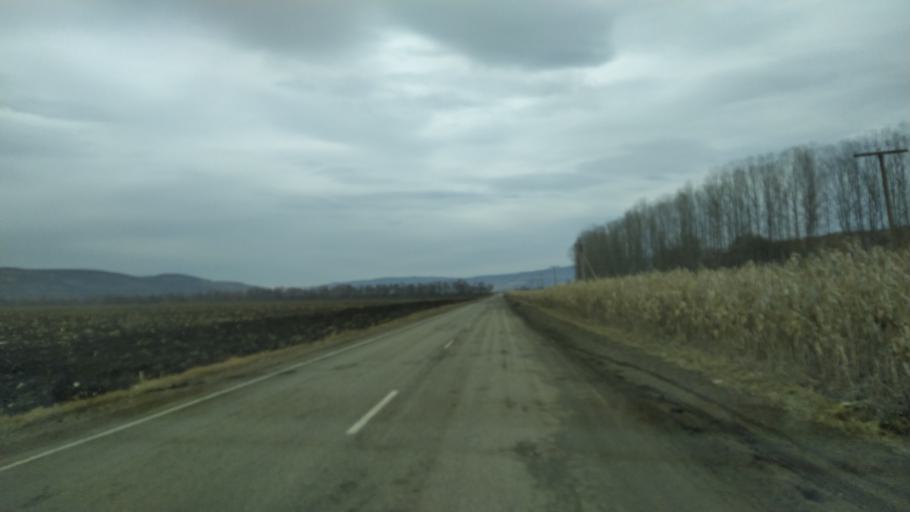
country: RU
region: Krasnodarskiy
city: Peredovaya
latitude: 44.1054
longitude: 41.4194
